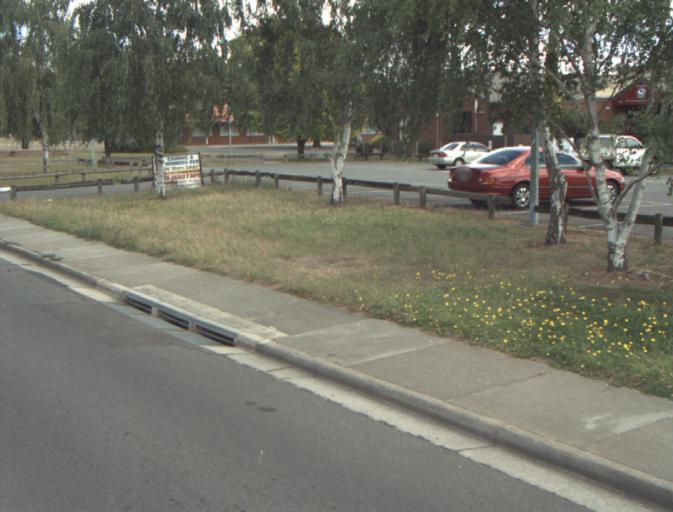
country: AU
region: Tasmania
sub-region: Launceston
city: Newstead
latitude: -41.4188
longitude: 147.1773
